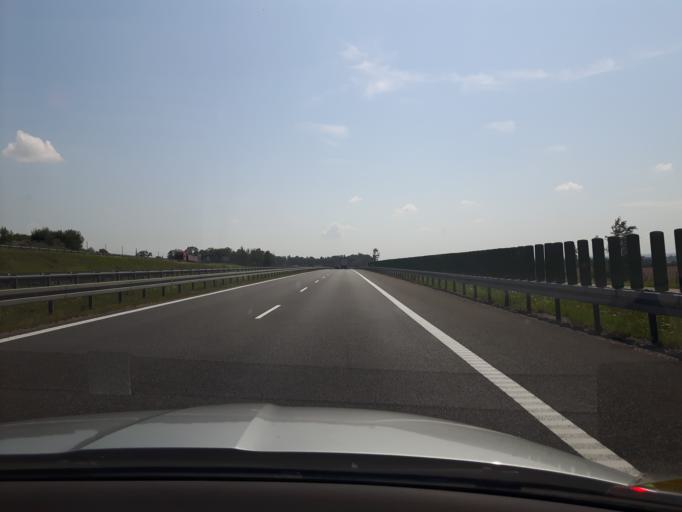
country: PL
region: Warmian-Masurian Voivodeship
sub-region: Powiat elblaski
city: Gronowo Gorne
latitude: 54.1182
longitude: 19.4741
